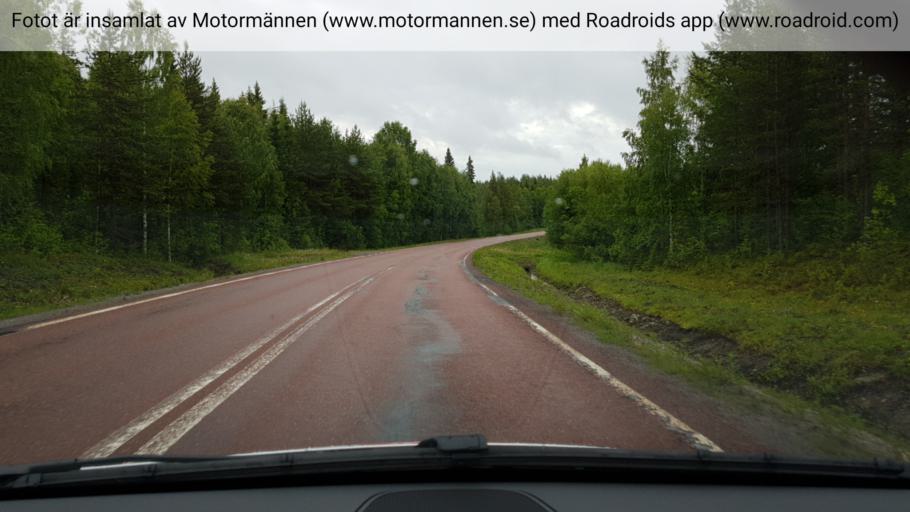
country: SE
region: Jaemtland
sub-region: Stroemsunds Kommun
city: Stroemsund
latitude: 64.0244
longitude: 15.9444
